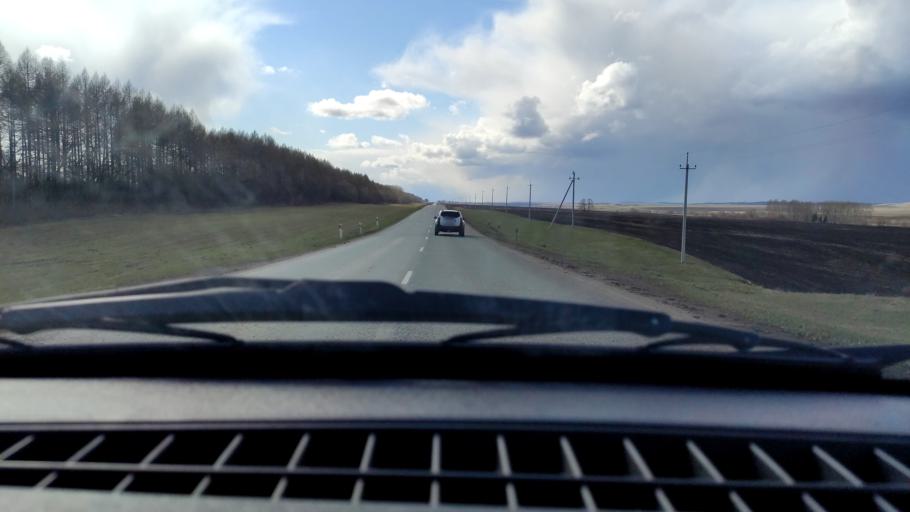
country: RU
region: Bashkortostan
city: Chekmagush
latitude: 55.1115
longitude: 54.9145
